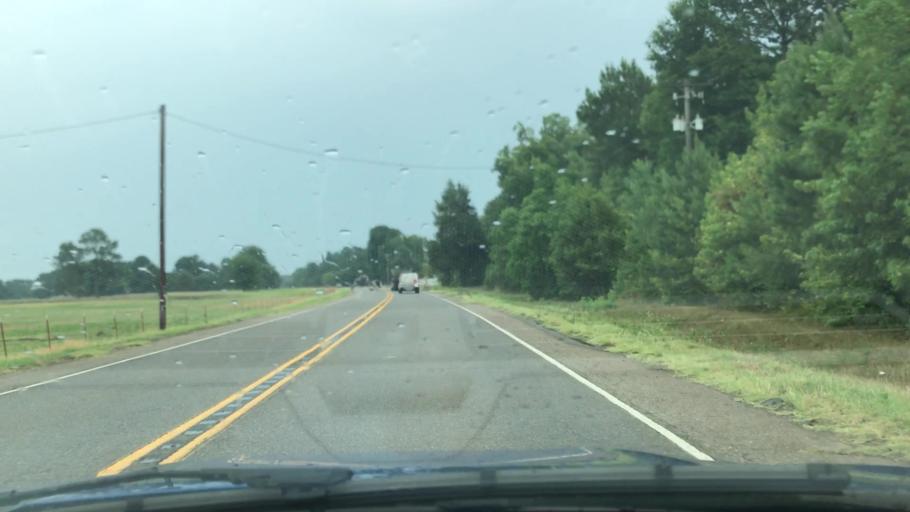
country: US
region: Texas
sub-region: Harrison County
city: Waskom
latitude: 32.4617
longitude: -94.0288
